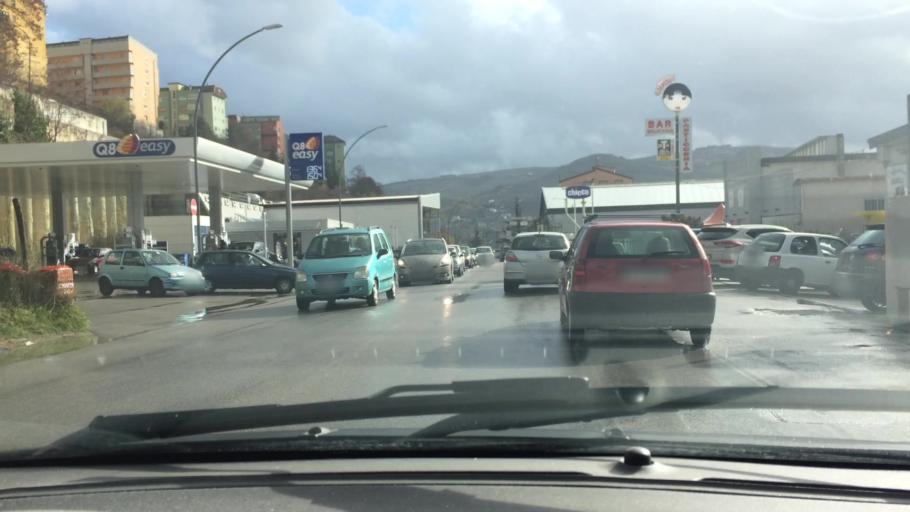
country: IT
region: Basilicate
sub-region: Provincia di Potenza
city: Potenza
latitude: 40.6318
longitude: 15.7891
